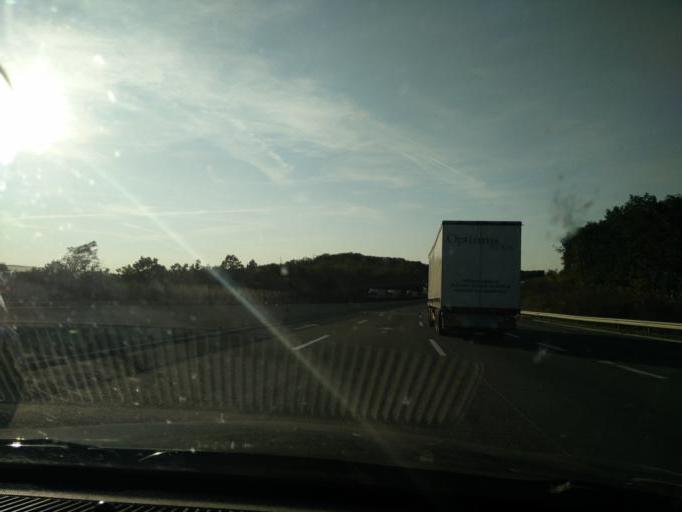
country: HU
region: Pest
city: Toeroekbalint
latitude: 47.4224
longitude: 18.9062
